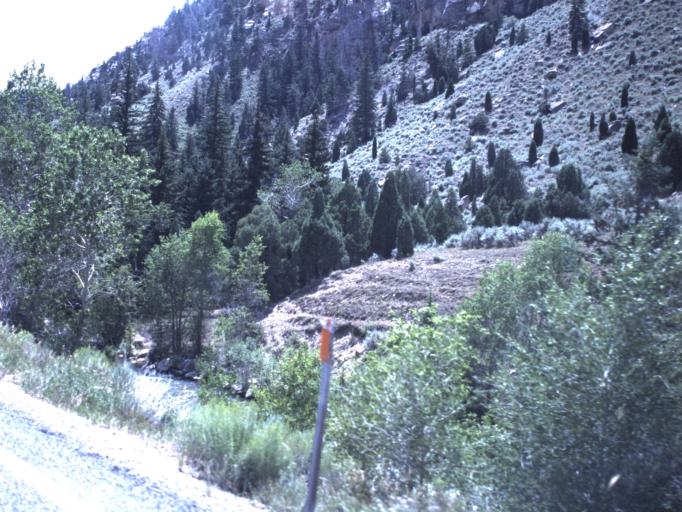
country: US
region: Utah
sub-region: Emery County
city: Huntington
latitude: 39.4371
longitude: -111.1327
